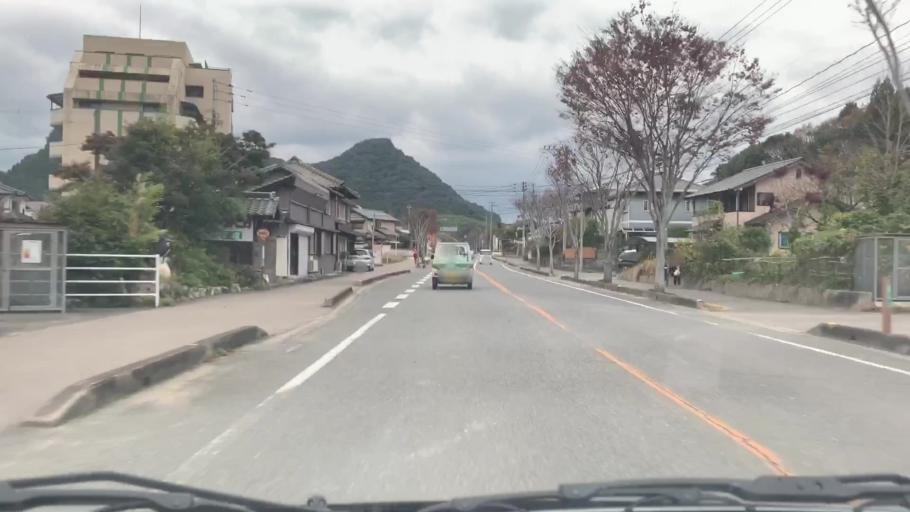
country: JP
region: Saga Prefecture
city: Takeocho-takeo
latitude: 33.1871
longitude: 130.0297
